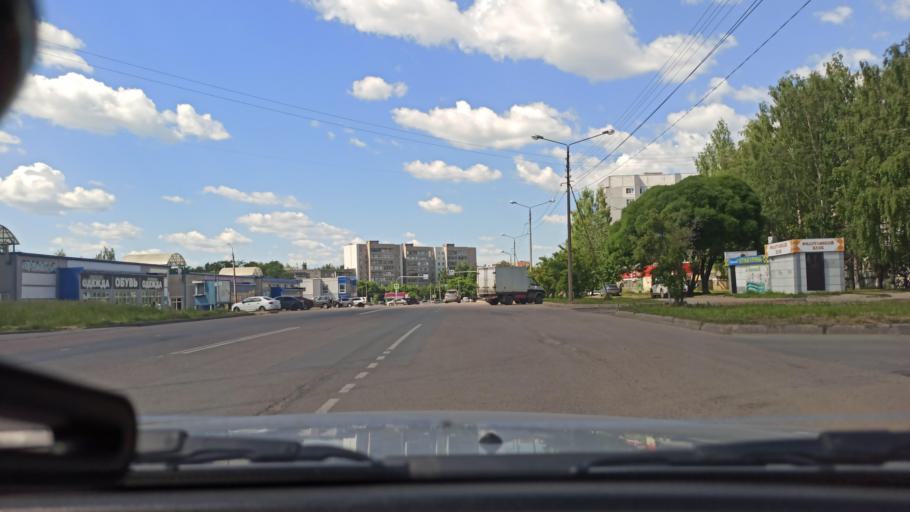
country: RU
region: Vologda
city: Vologda
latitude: 59.1944
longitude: 39.8645
